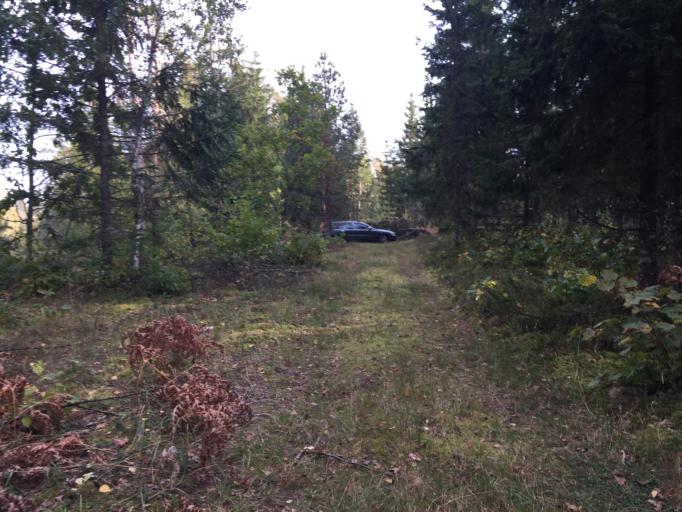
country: LV
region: Garkalne
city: Garkalne
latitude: 56.9737
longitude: 24.4260
